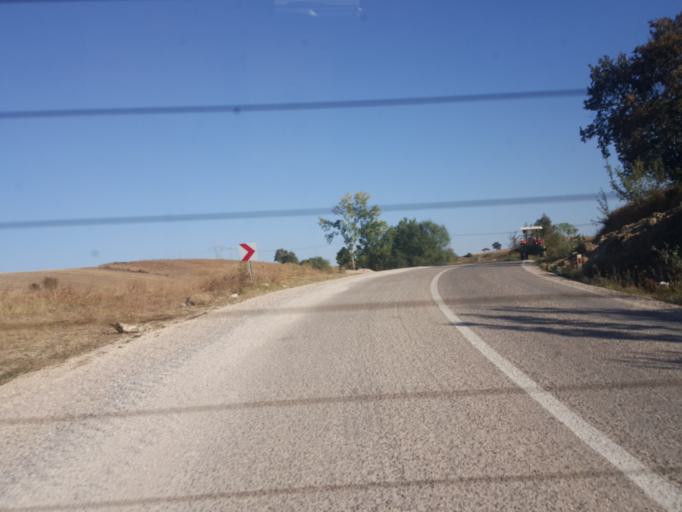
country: TR
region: Amasya
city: Tasova
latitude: 40.7129
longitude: 36.3313
